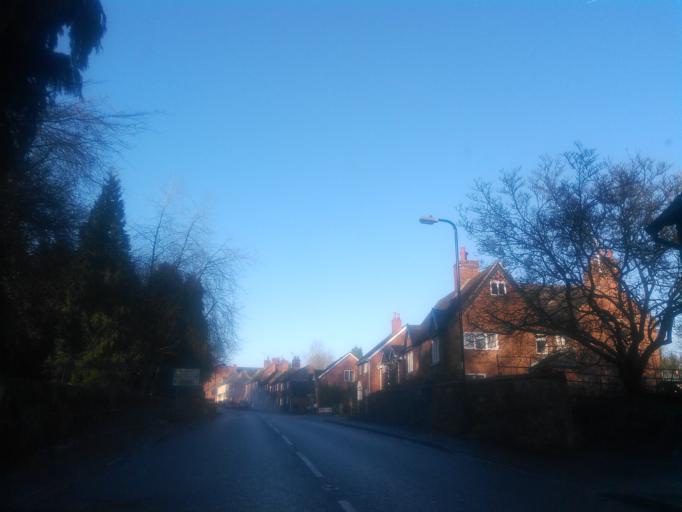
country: GB
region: England
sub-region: Shropshire
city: Stoke upon Tern
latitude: 52.8520
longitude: -2.5739
